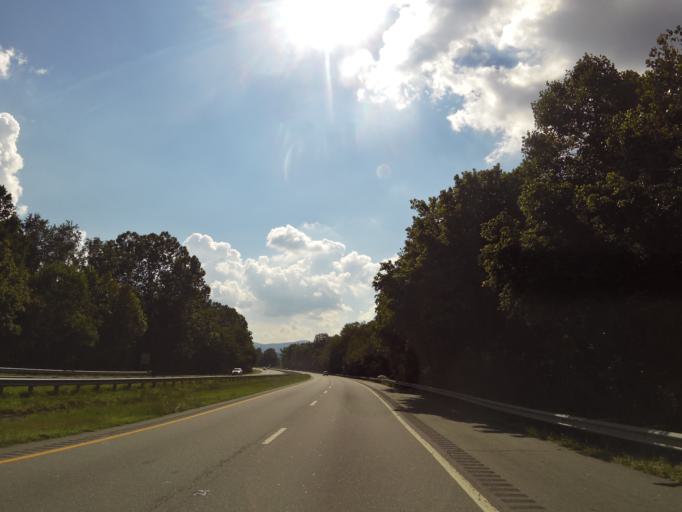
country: US
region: North Carolina
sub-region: McDowell County
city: West Marion
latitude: 35.6382
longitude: -82.1578
